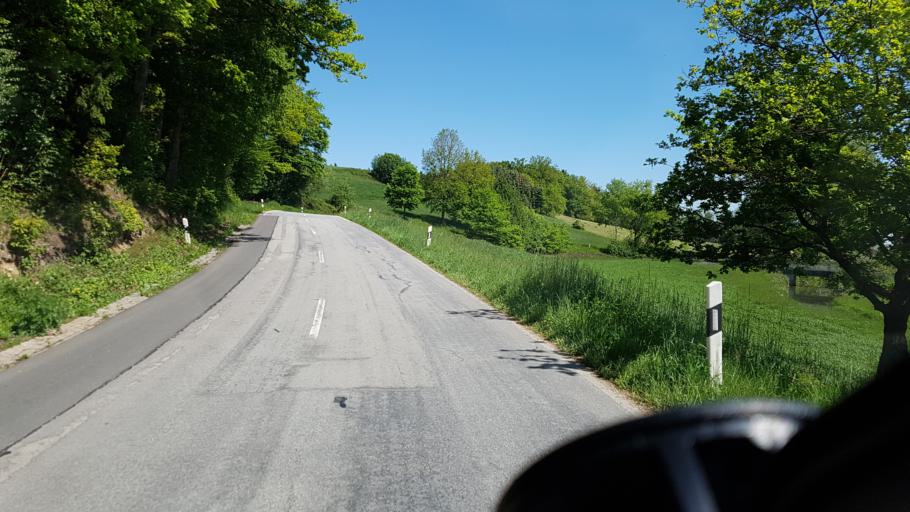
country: DE
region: Bavaria
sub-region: Lower Bavaria
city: Postmunster
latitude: 48.3710
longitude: 12.8961
